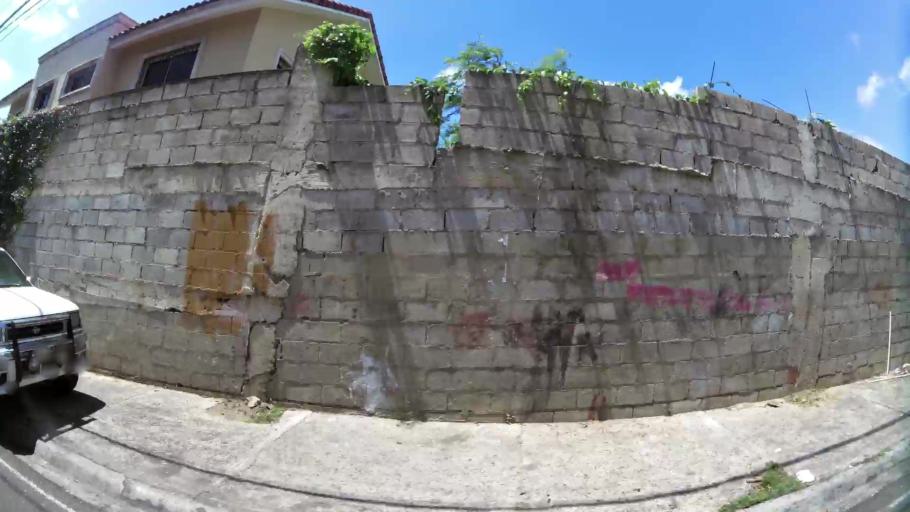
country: DO
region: Santiago
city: Santiago de los Caballeros
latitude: 19.4666
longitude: -70.6755
